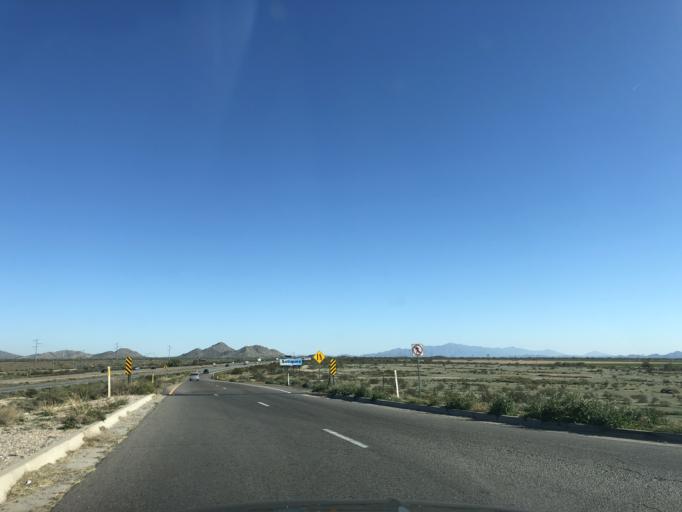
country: US
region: Arizona
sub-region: Maricopa County
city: Buckeye
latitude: 33.4383
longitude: -112.6772
